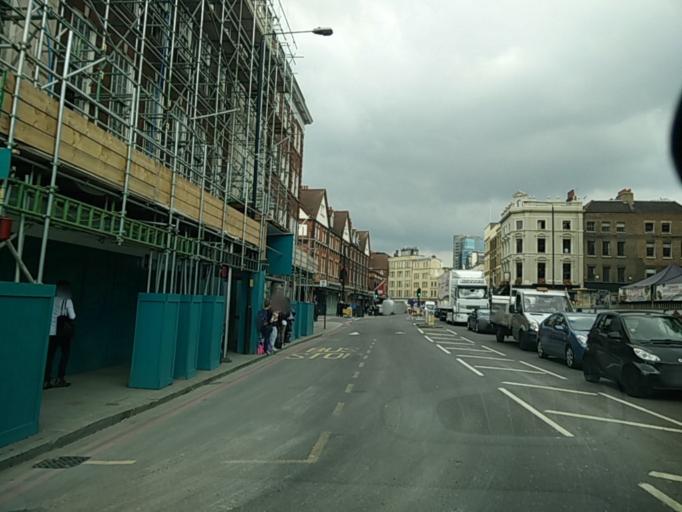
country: GB
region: England
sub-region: Greater London
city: Bethnal Green
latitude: 51.5186
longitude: -0.0744
